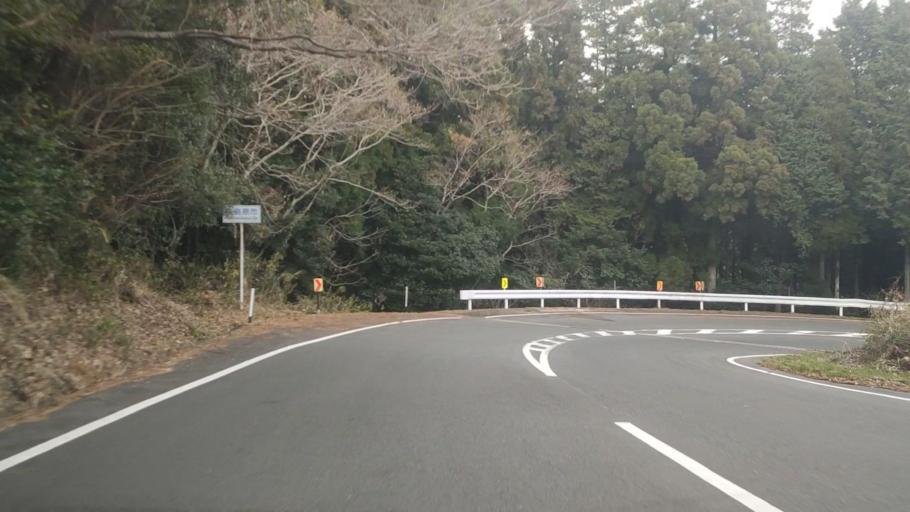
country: JP
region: Nagasaki
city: Shimabara
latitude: 32.7183
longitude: 130.2481
